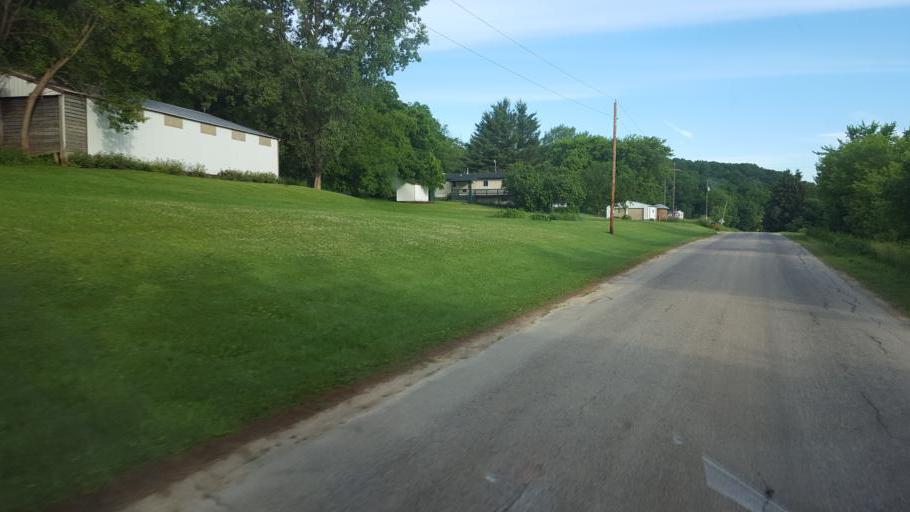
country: US
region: Wisconsin
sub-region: Vernon County
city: Hillsboro
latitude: 43.5928
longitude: -90.3625
